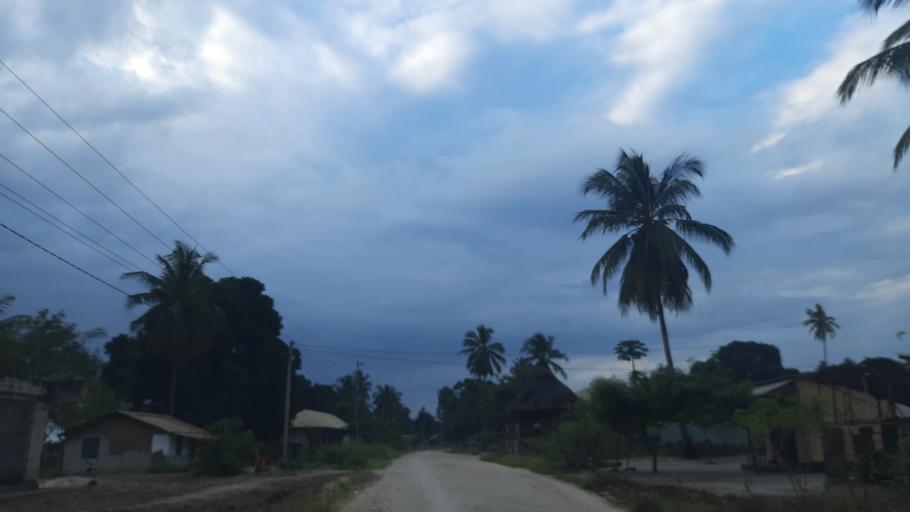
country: TZ
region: Pwani
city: Bagamoyo
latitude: -6.5118
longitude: 38.9310
